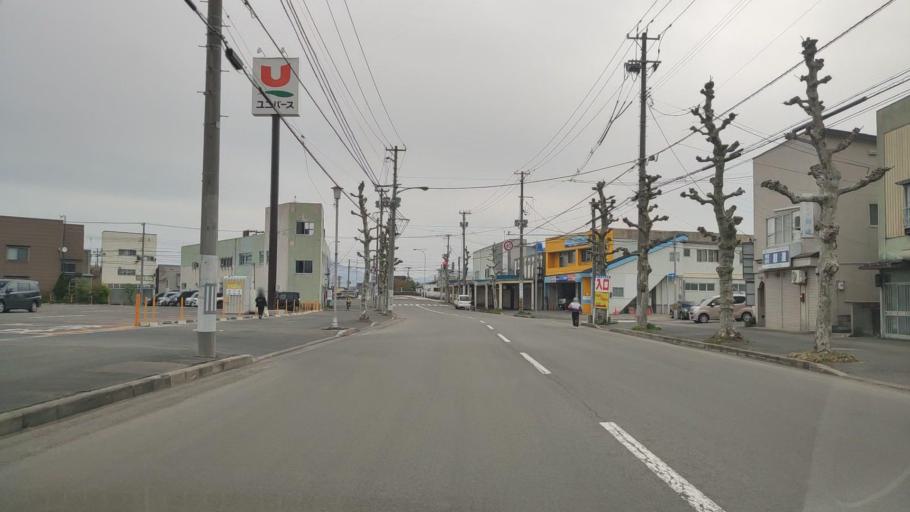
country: JP
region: Aomori
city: Aomori Shi
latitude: 40.8257
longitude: 140.7590
